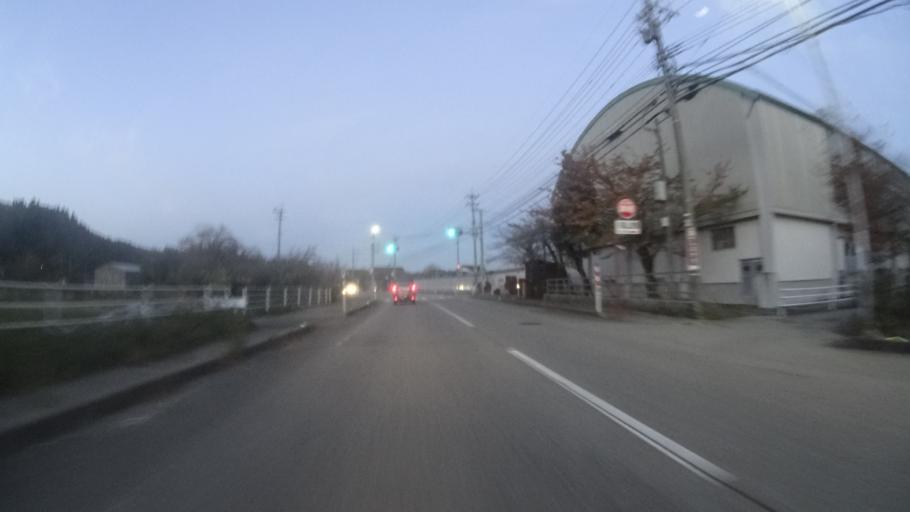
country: JP
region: Ishikawa
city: Nanao
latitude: 37.3830
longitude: 136.8879
